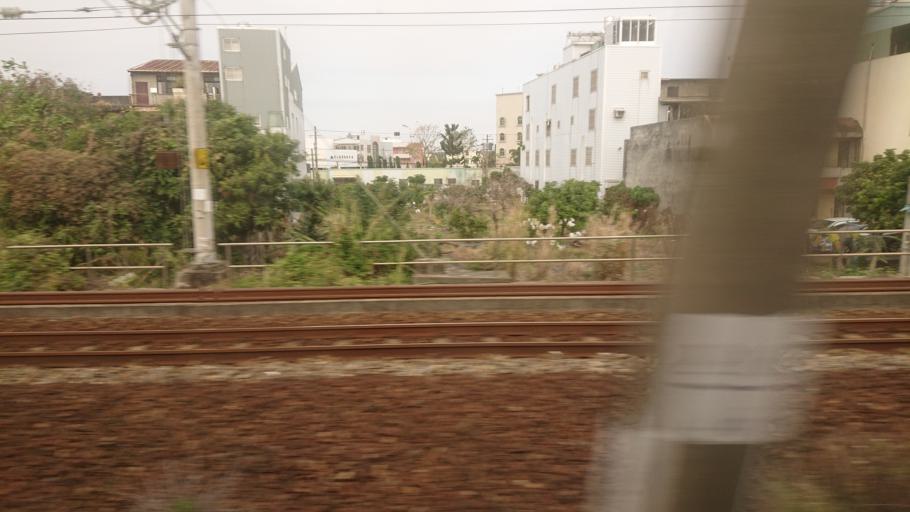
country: TW
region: Taiwan
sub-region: Changhua
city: Chang-hua
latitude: 24.0980
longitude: 120.5717
